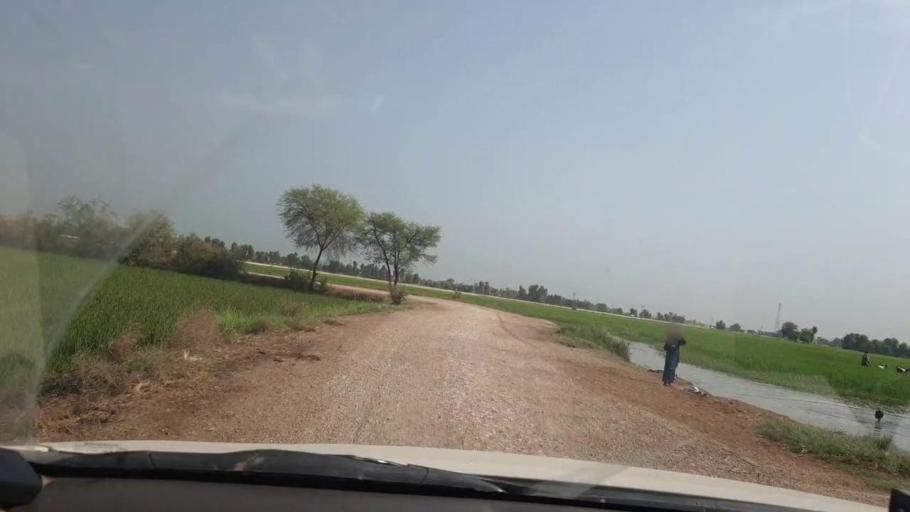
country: PK
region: Sindh
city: Chak
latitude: 27.8400
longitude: 68.7995
